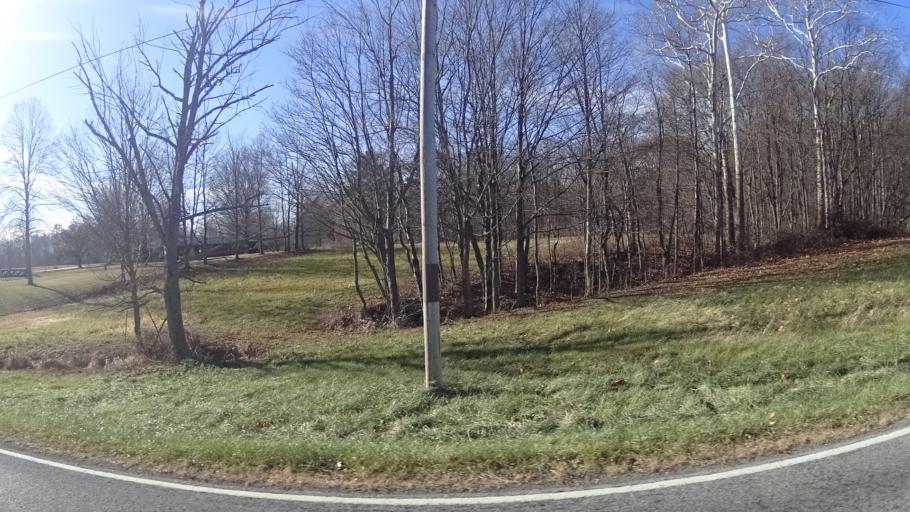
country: US
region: Ohio
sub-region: Lorain County
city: Camden
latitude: 41.3033
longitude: -82.3355
